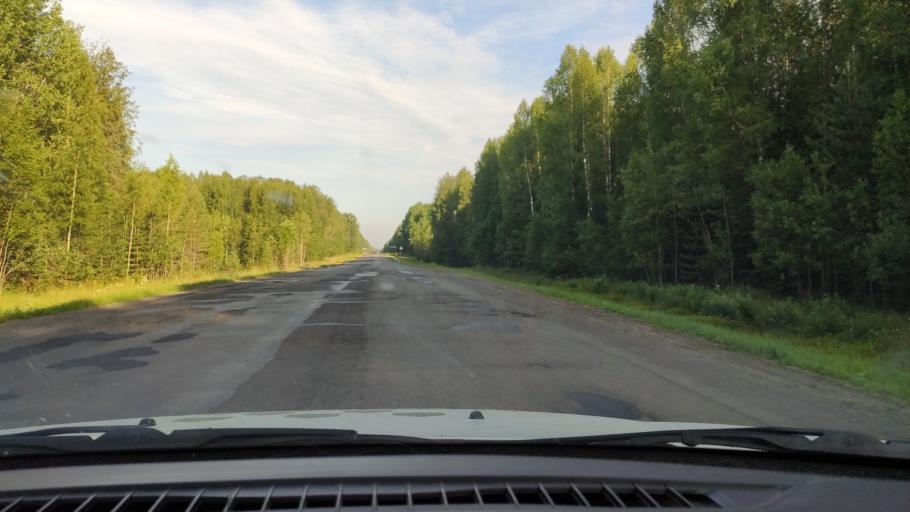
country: RU
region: Kirov
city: Omutninsk
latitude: 58.7668
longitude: 51.9772
